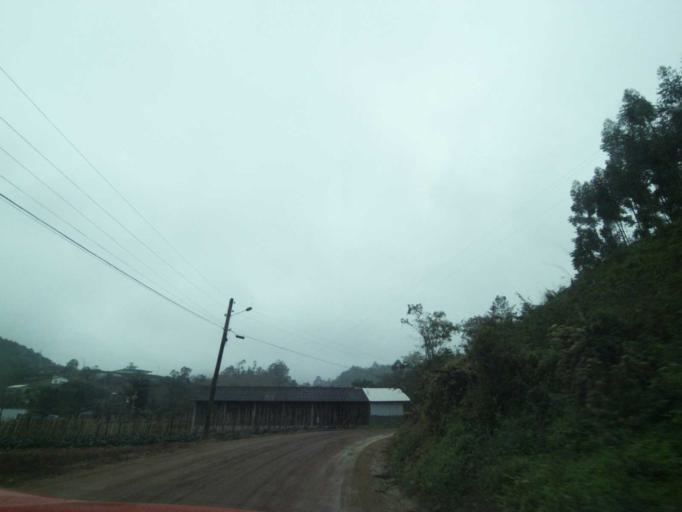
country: BR
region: Santa Catarina
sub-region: Anitapolis
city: Anitapolis
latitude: -27.9120
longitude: -49.1325
